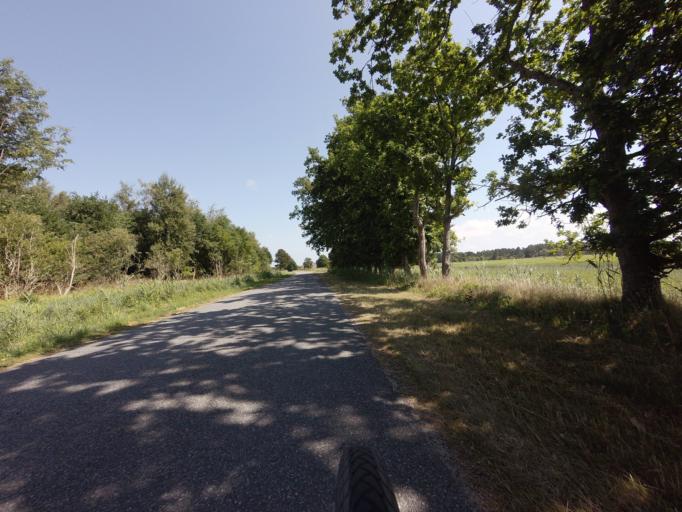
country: DK
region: North Denmark
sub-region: Laeso Kommune
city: Byrum
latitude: 57.2520
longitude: 10.9599
